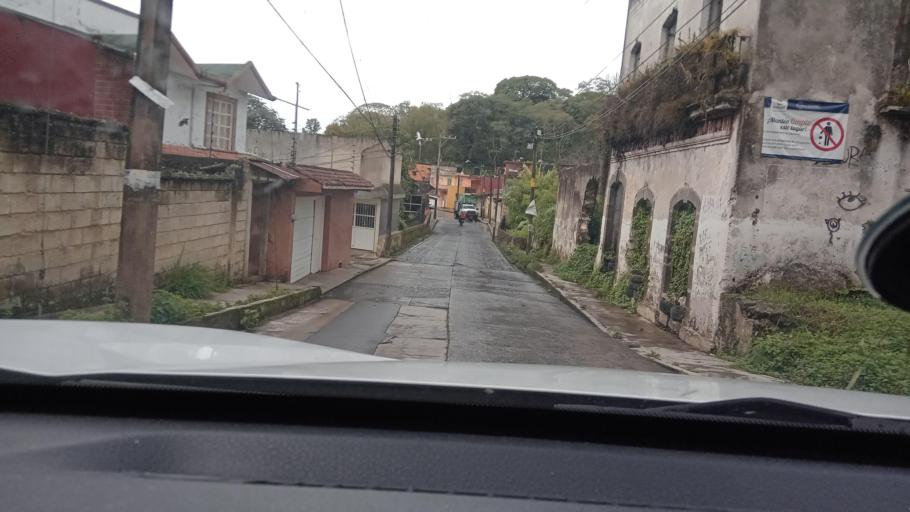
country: MX
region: Veracruz
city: Coatepec
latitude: 19.4464
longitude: -96.9588
